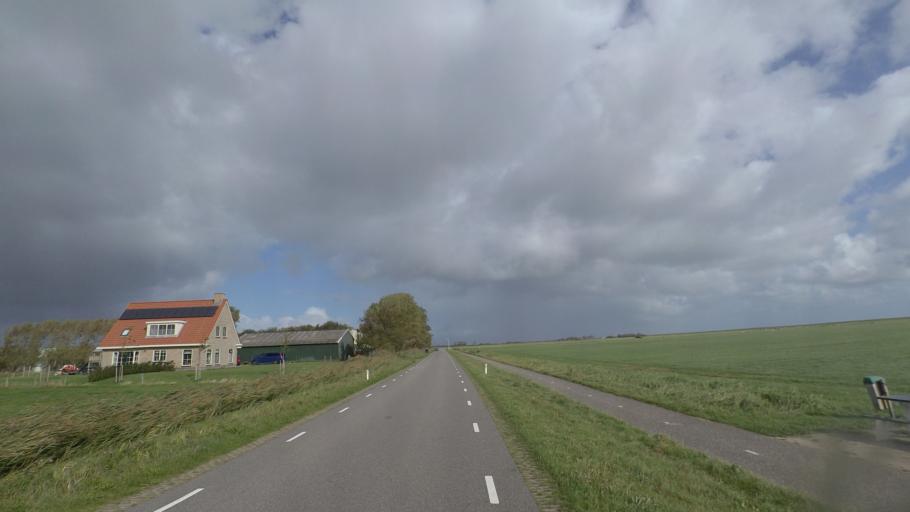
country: NL
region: Friesland
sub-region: Gemeente Ameland
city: Hollum
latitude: 53.4371
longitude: 5.6695
